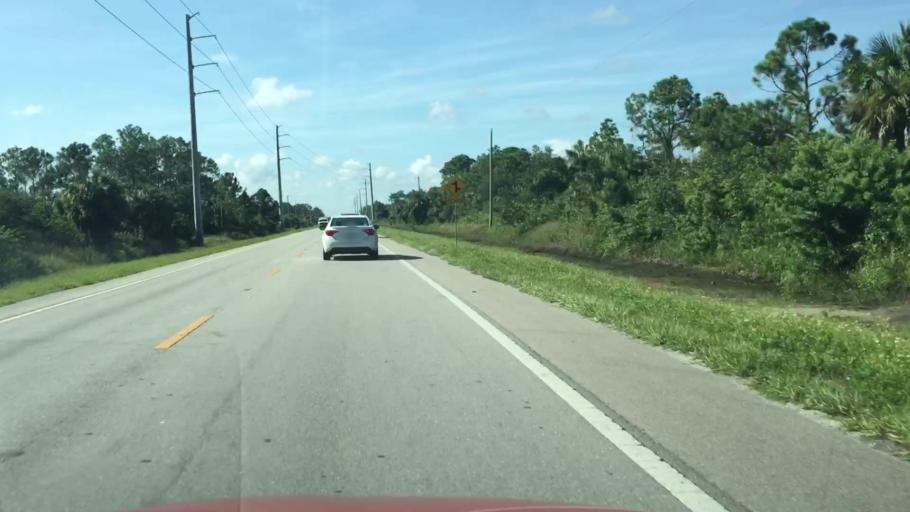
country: US
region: Florida
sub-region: Collier County
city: Orangetree
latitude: 26.3220
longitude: -81.5951
